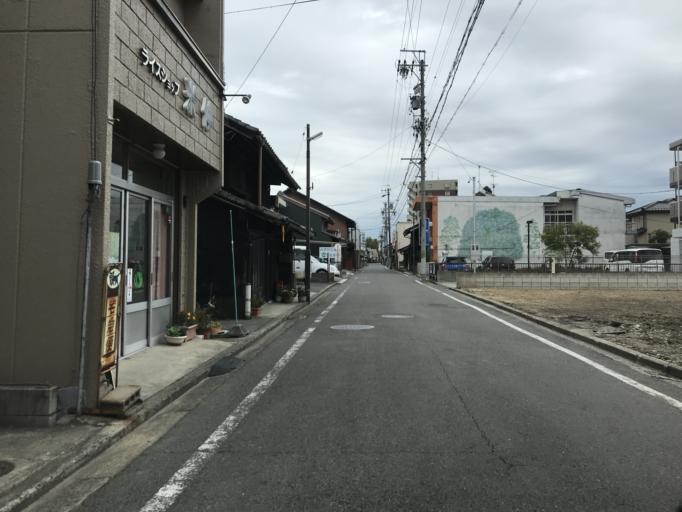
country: JP
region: Aichi
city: Nagoya-shi
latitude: 35.1928
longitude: 136.8564
